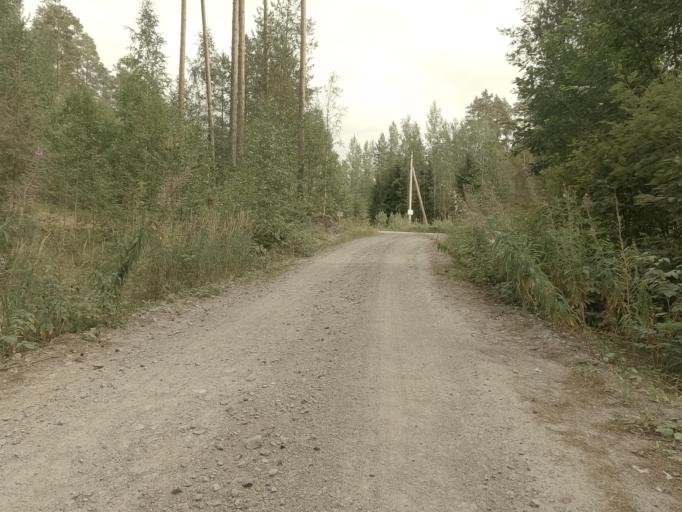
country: RU
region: Leningrad
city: Kamennogorsk
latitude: 60.9743
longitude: 29.1771
